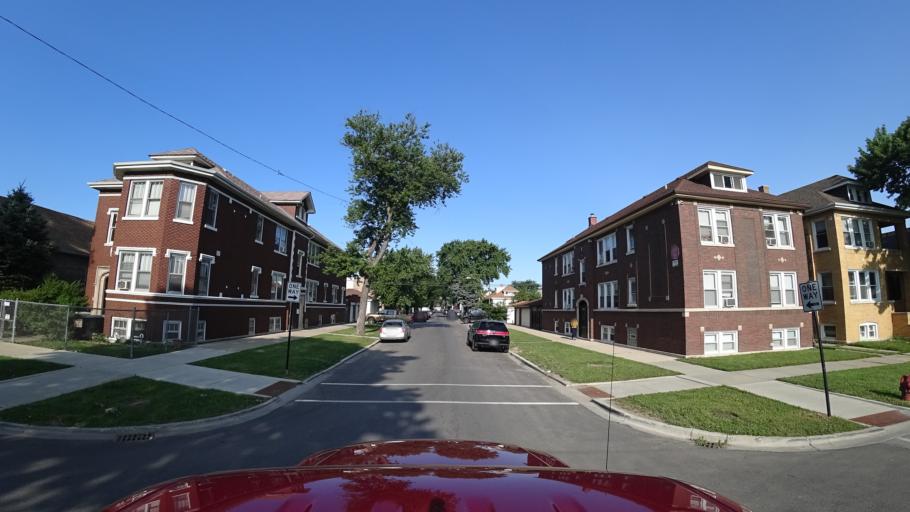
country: US
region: Illinois
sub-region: Cook County
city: Hometown
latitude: 41.7953
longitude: -87.7048
